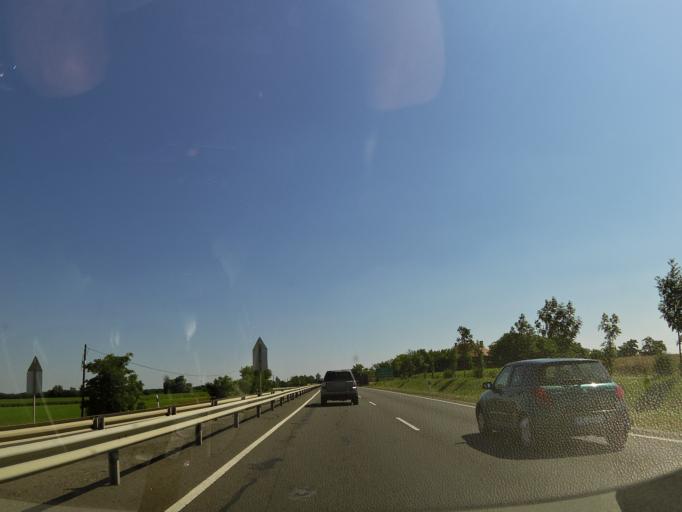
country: HU
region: Jasz-Nagykun-Szolnok
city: Torokszentmiklos
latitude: 47.1960
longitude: 20.4661
